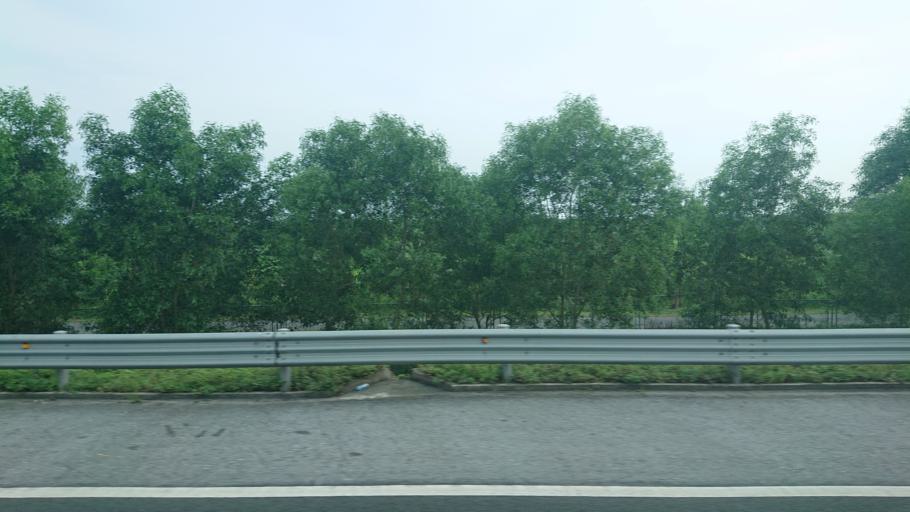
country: VN
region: Hai Duong
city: Tu Ky
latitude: 20.8268
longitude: 106.4596
